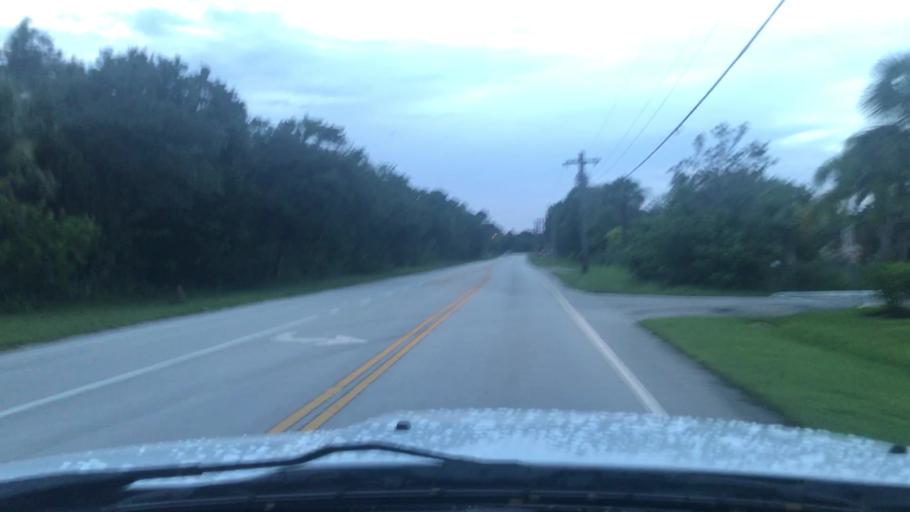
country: US
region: Florida
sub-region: Indian River County
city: Florida Ridge
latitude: 27.5919
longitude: -80.3814
